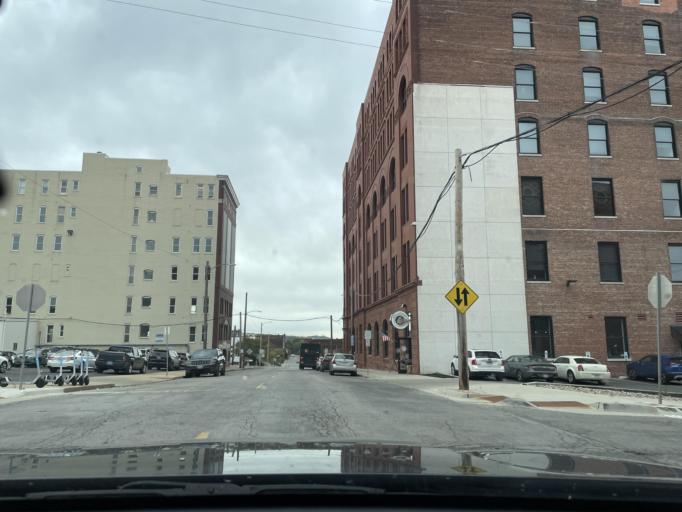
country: US
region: Missouri
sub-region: Buchanan County
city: Saint Joseph
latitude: 39.7690
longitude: -94.8568
